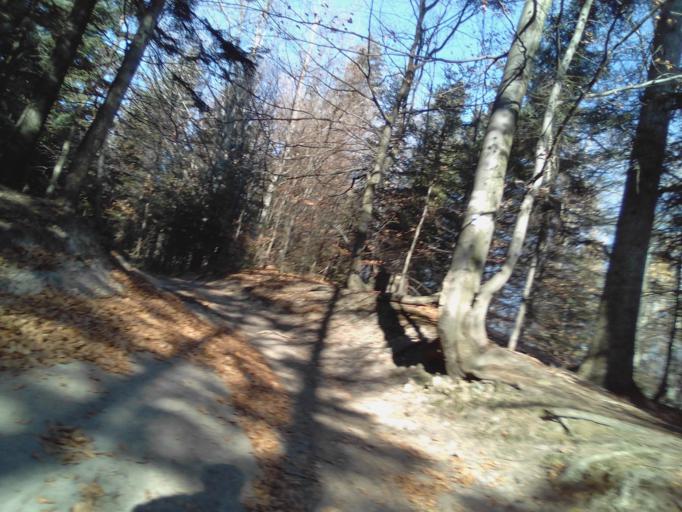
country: PL
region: Subcarpathian Voivodeship
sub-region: Powiat strzyzowski
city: Wysoka Strzyzowska
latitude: 49.8105
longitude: 21.7178
